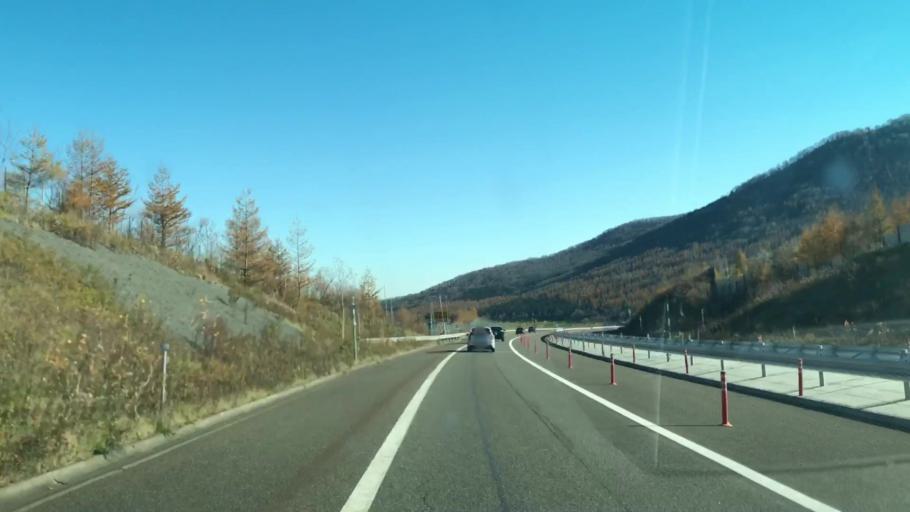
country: JP
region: Hokkaido
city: Otofuke
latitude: 43.0294
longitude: 142.8051
